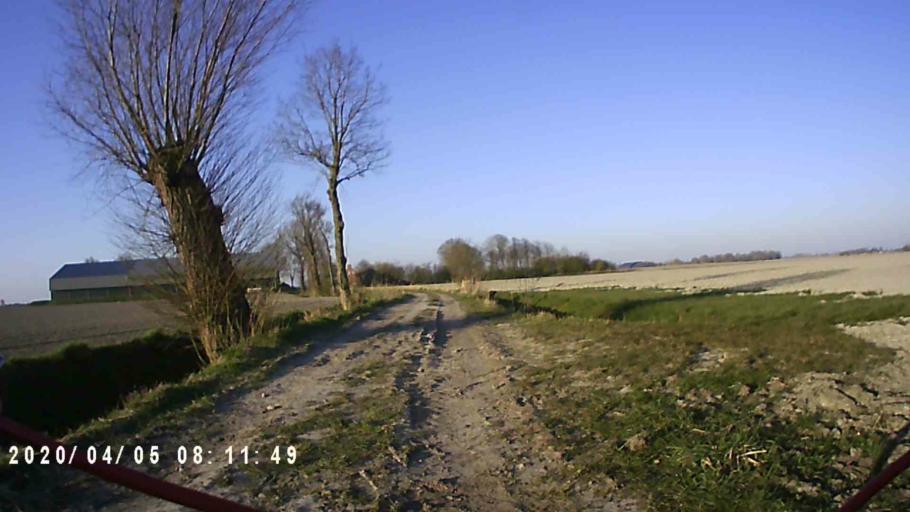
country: NL
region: Groningen
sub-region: Gemeente Zuidhorn
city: Oldehove
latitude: 53.3471
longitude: 6.4451
